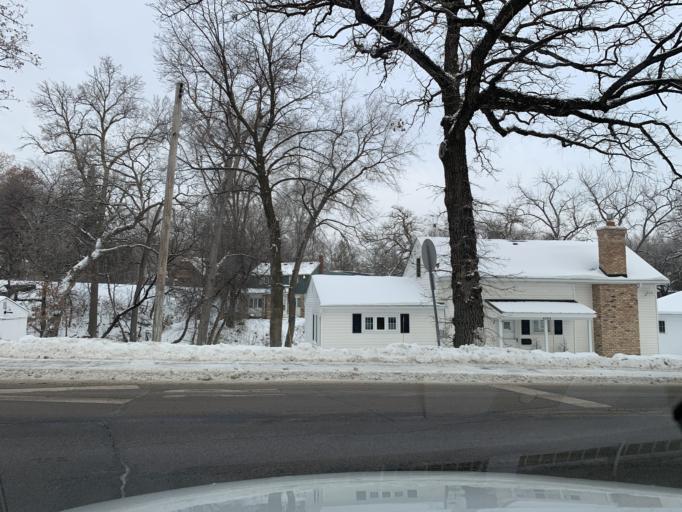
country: US
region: Minnesota
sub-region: Hennepin County
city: Saint Louis Park
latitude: 44.9211
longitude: -93.3532
